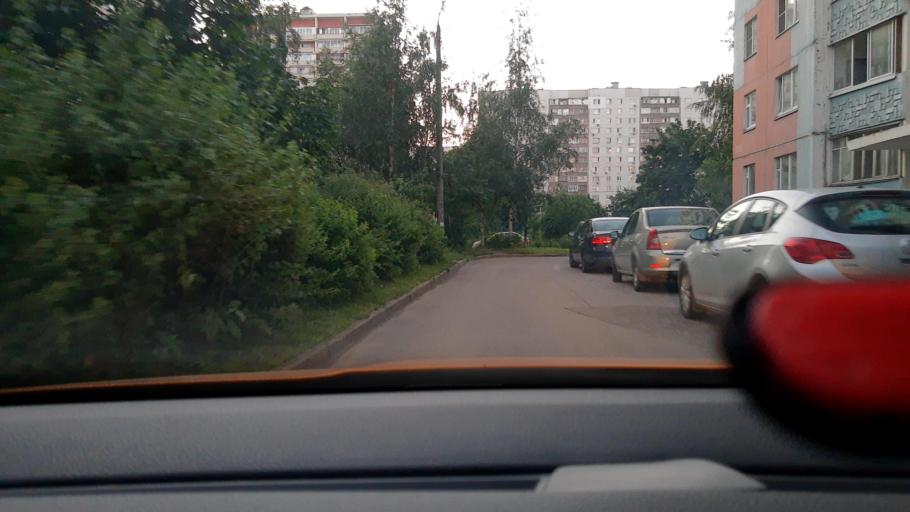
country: RU
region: Moskovskaya
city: Yubileyny
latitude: 55.9081
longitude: 37.8704
